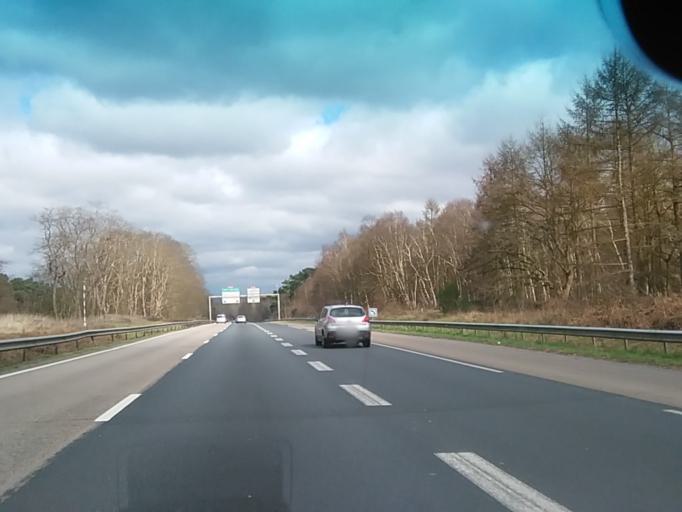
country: FR
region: Haute-Normandie
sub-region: Departement de la Seine-Maritime
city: Le Grand-Quevilly
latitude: 49.3723
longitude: 1.0442
